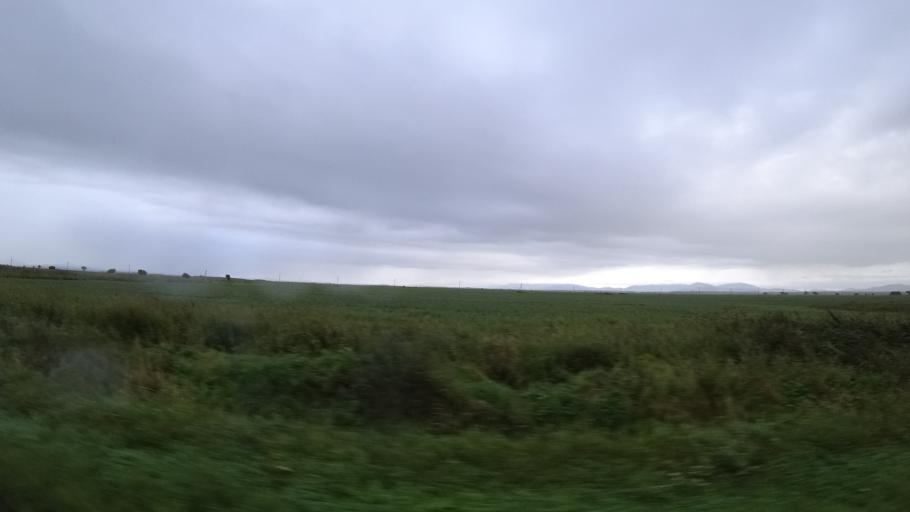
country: RU
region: Primorskiy
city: Chernigovka
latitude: 44.3867
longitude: 132.5295
